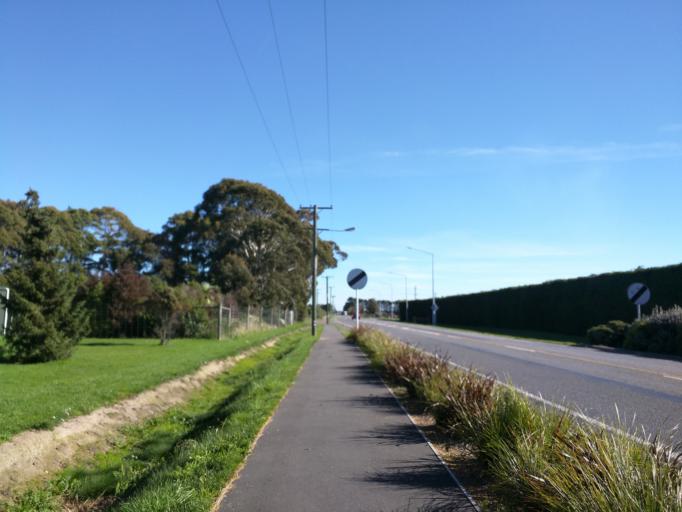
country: NZ
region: Canterbury
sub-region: Selwyn District
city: Lincoln
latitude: -43.6433
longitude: 172.4595
